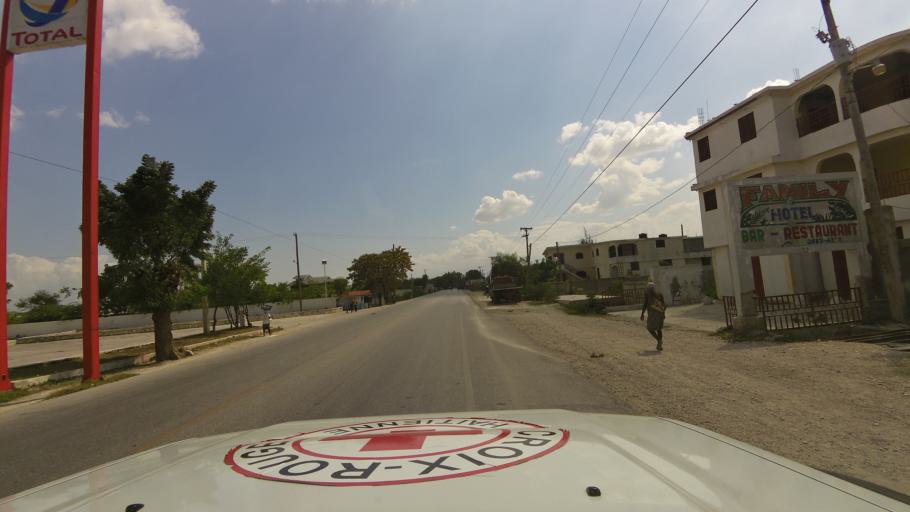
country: HT
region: Ouest
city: Croix des Bouquets
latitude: 18.6408
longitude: -72.2713
